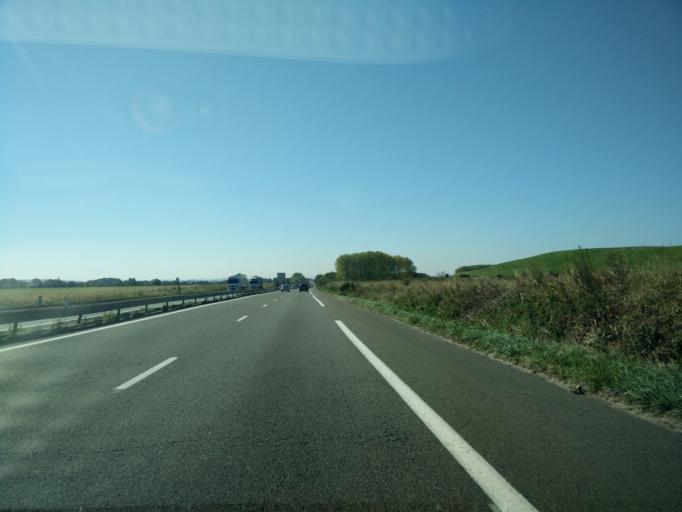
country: FR
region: Ile-de-France
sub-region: Departement de Seine-et-Marne
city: Mitry-Mory
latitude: 48.9941
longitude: 2.6247
